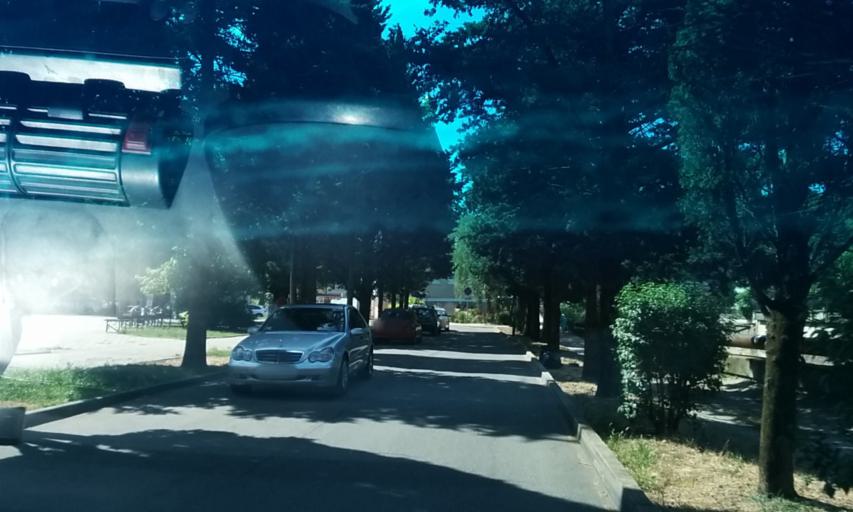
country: RU
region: Krasnodarskiy
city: Tuapse
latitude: 44.1071
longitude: 39.0599
